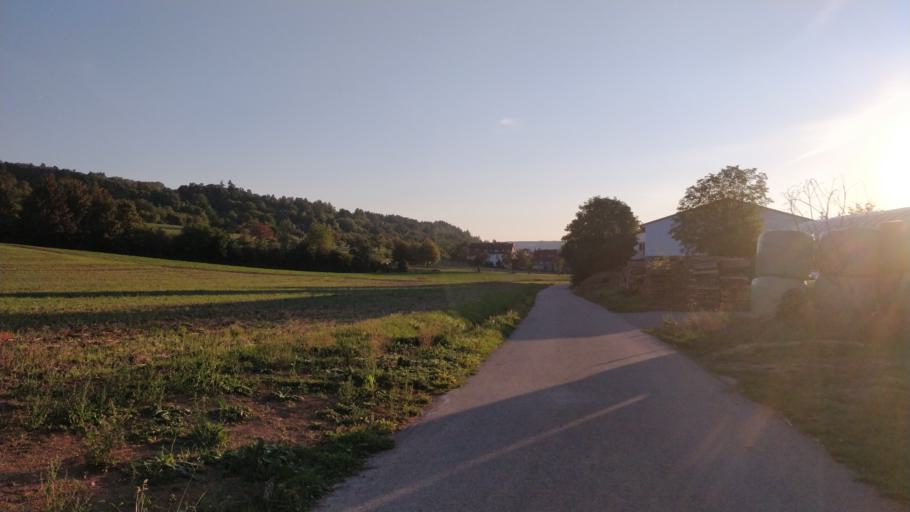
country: DE
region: Baden-Wuerttemberg
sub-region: Karlsruhe Region
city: Heimsheim
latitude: 48.8075
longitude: 8.8759
